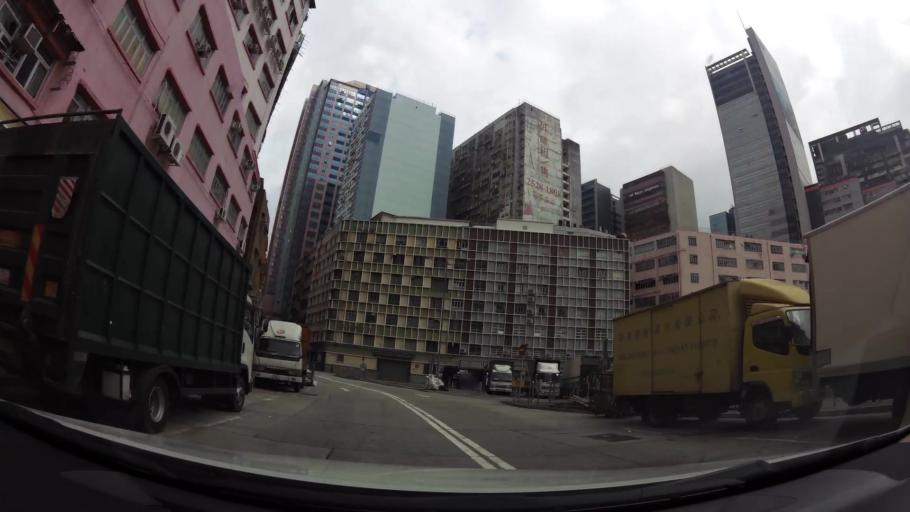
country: HK
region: Wong Tai Sin
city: Wong Tai Sin
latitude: 22.3354
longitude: 114.1983
